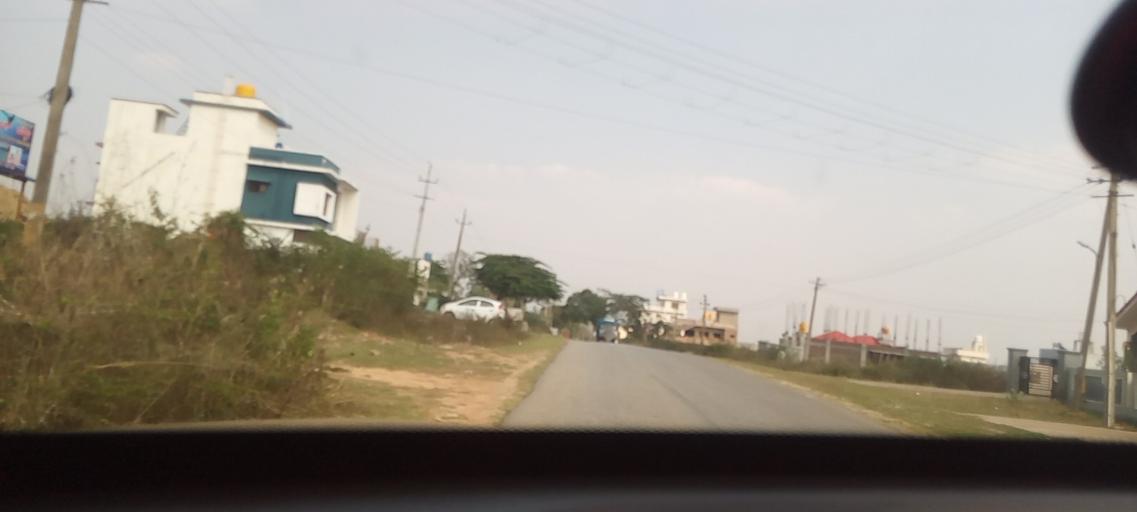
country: IN
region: Karnataka
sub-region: Hassan
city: Belur
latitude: 13.1745
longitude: 75.8534
